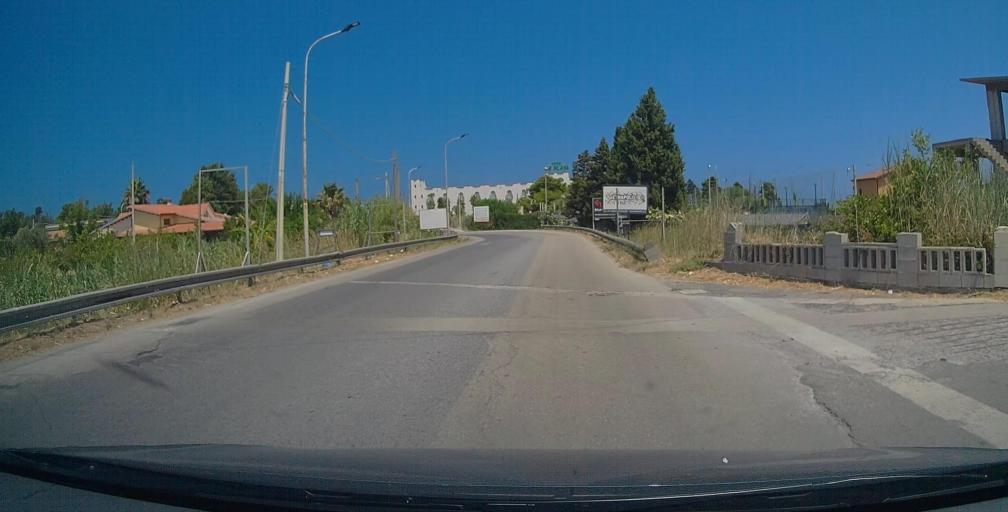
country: IT
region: Sicily
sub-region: Messina
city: Patti
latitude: 38.1475
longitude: 14.9807
